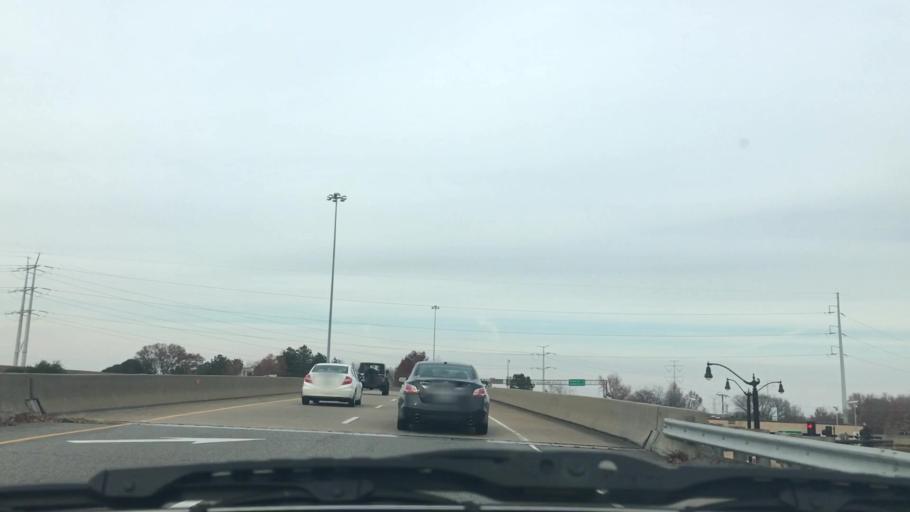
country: US
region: Virginia
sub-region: City of Newport News
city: Newport News
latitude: 36.9882
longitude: -76.4258
